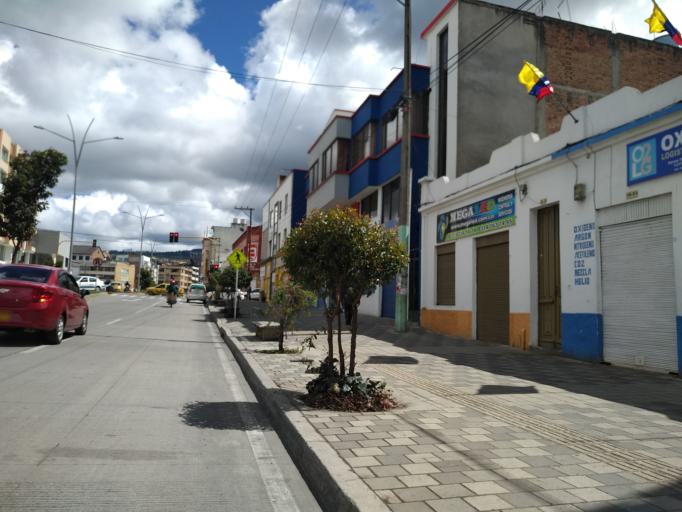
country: CO
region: Narino
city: Pasto
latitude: 1.2094
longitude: -77.2750
